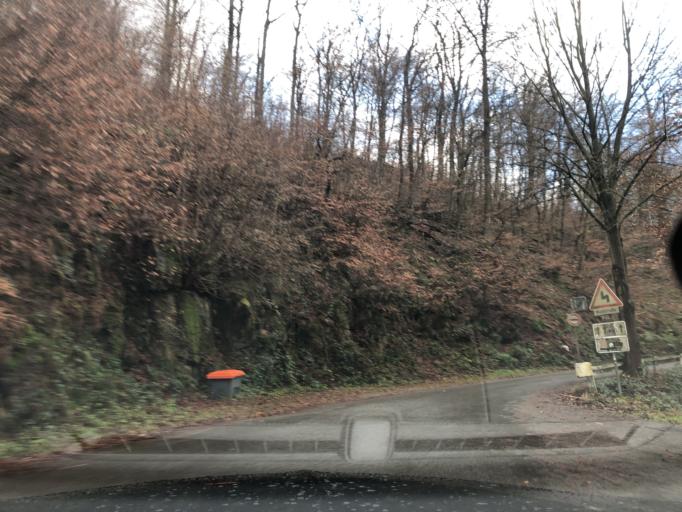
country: DE
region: Baden-Wuerttemberg
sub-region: Karlsruhe Region
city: Dossenheim
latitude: 49.4504
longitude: 8.6874
